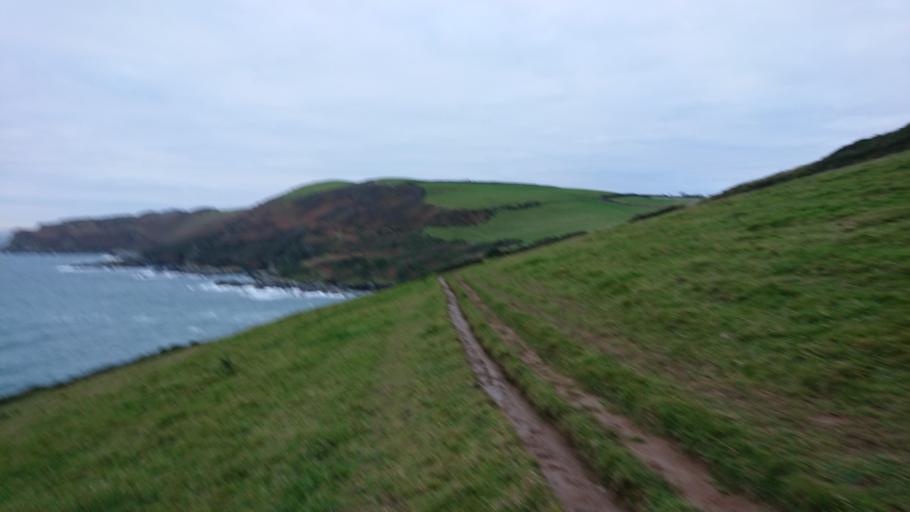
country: GB
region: England
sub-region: Cornwall
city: Fowey
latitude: 50.3323
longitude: -4.5815
